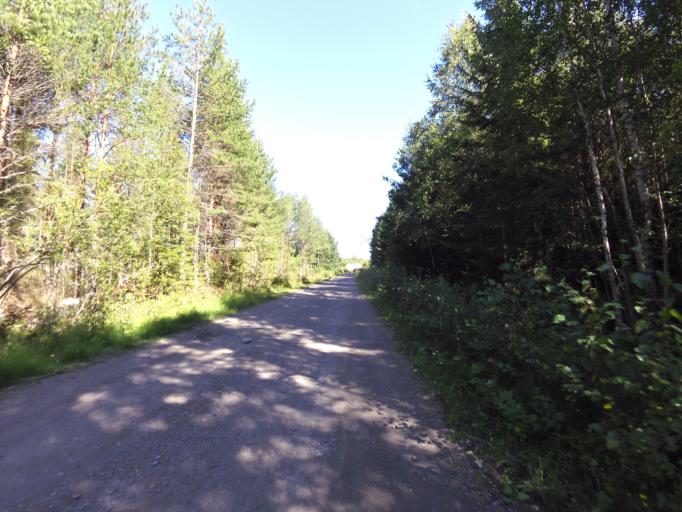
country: SE
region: Gaevleborg
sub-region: Hofors Kommun
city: Hofors
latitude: 60.5104
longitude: 16.3457
